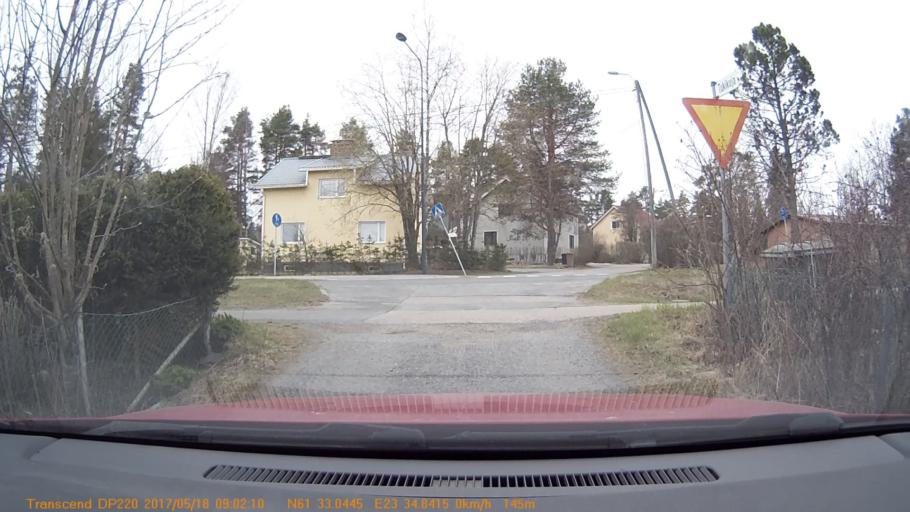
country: FI
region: Pirkanmaa
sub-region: Tampere
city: Yloejaervi
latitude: 61.5507
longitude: 23.5807
